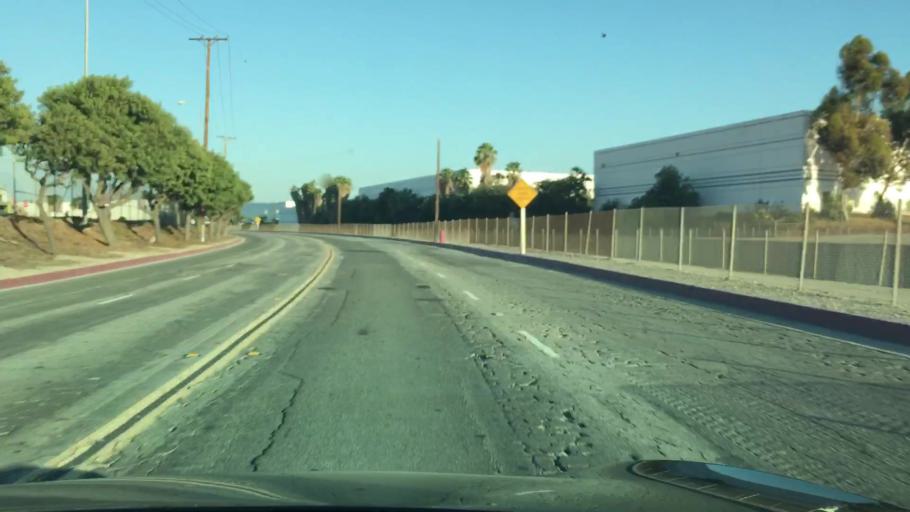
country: US
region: California
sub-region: Los Angeles County
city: South San Jose Hills
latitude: 34.0058
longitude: -117.9224
